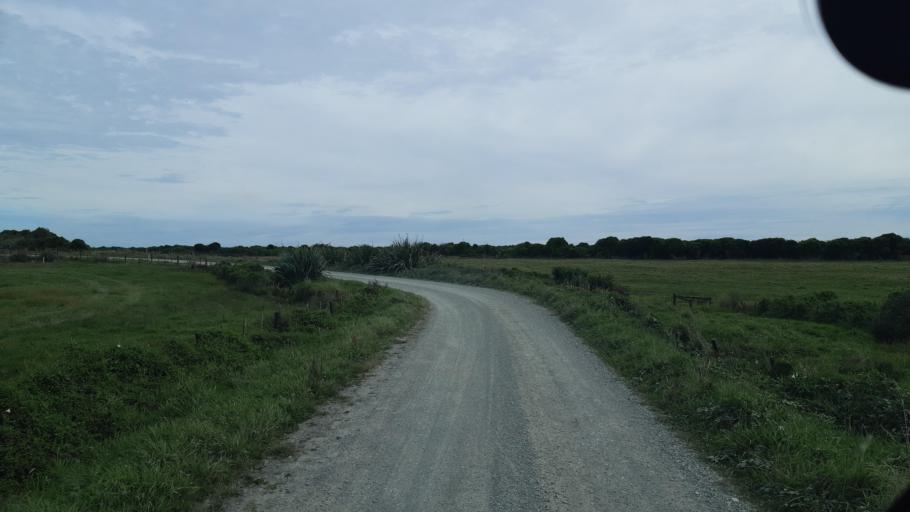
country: NZ
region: West Coast
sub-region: Westland District
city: Hokitika
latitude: -42.9081
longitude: 170.7551
